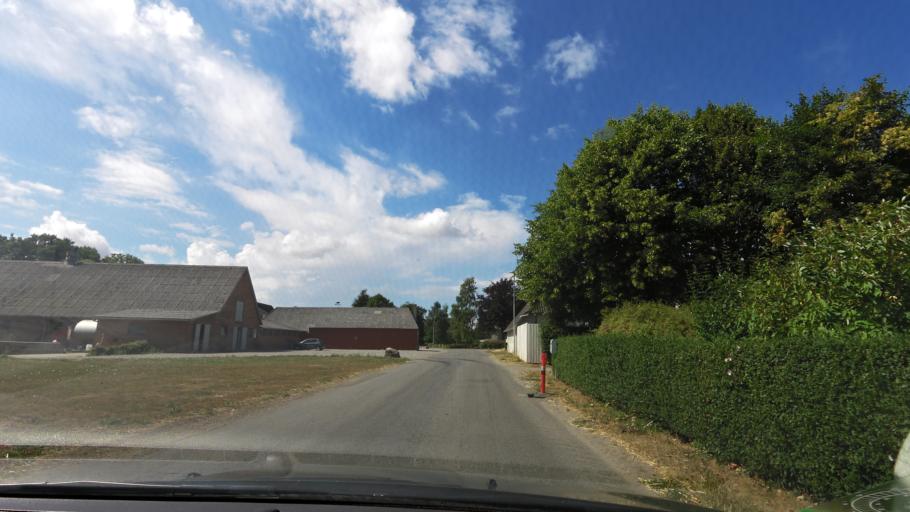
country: DK
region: South Denmark
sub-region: Nordfyns Kommune
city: Otterup
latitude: 55.5487
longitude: 10.4491
